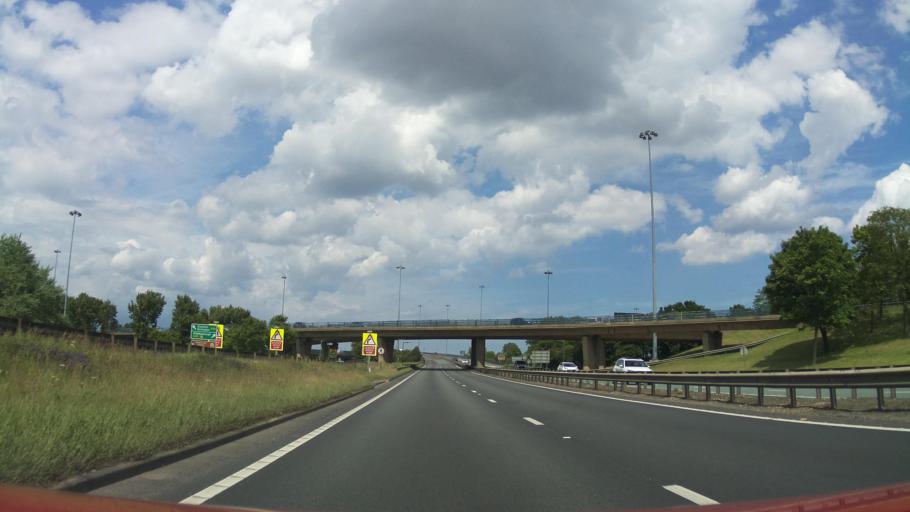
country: GB
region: England
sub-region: Stockton-on-Tees
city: Billingham
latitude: 54.5609
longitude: -1.2686
